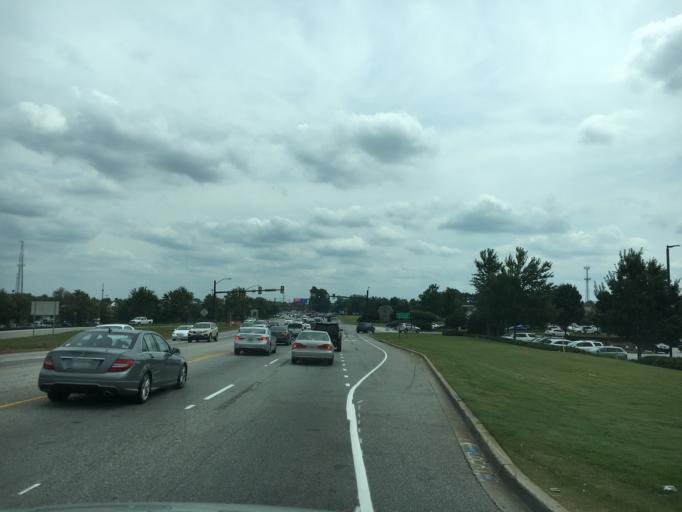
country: US
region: South Carolina
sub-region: Greenville County
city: Mauldin
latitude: 34.8284
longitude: -82.3021
